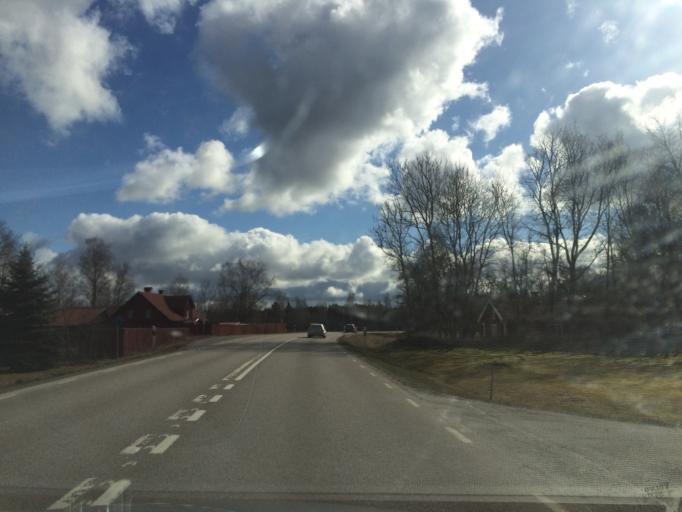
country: SE
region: Vaestra Goetaland
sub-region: Skara Kommun
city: Skara
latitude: 58.3296
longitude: 13.4363
